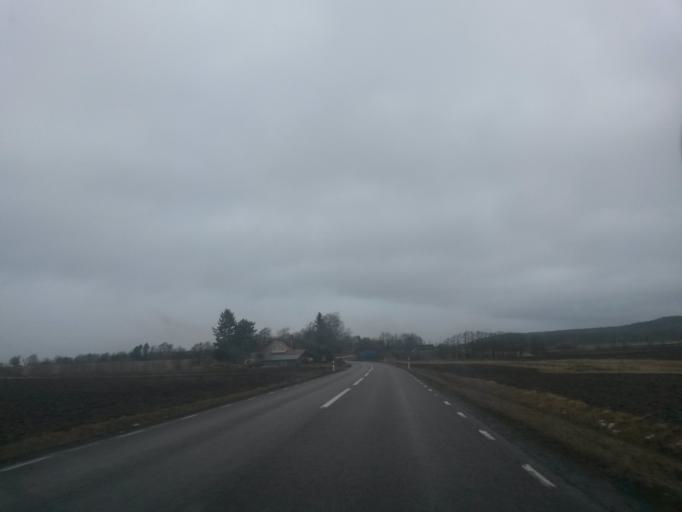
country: SE
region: Vaestra Goetaland
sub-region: Vanersborgs Kommun
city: Vargon
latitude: 58.2856
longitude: 12.3953
